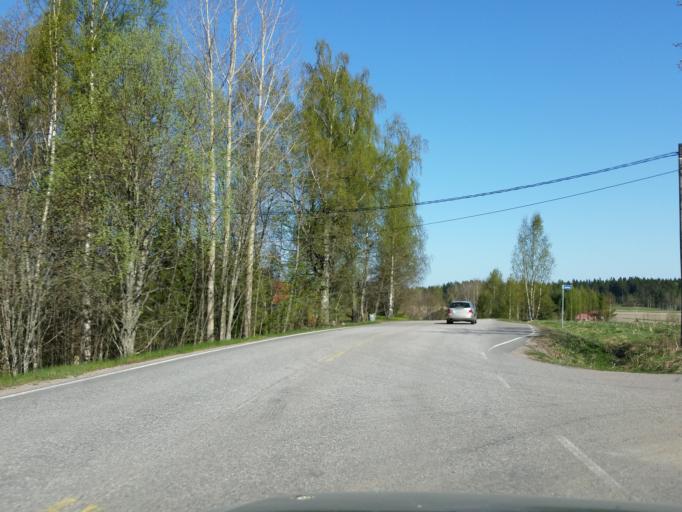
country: FI
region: Uusimaa
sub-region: Helsinki
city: Kirkkonummi
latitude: 60.1970
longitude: 24.3847
